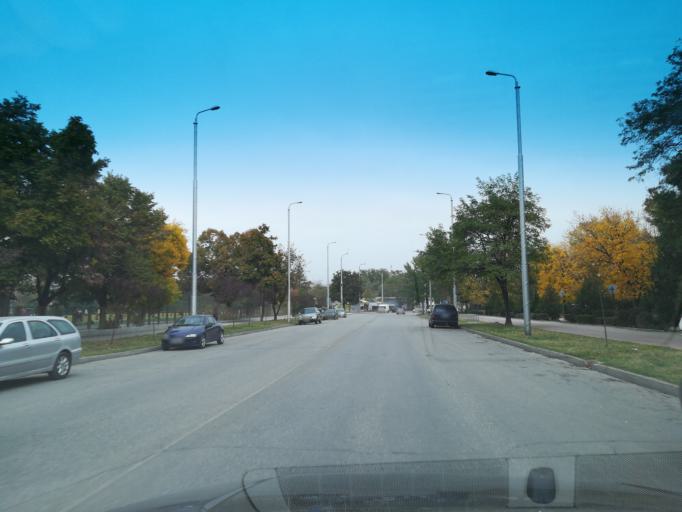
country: BG
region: Plovdiv
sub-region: Obshtina Plovdiv
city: Plovdiv
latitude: 42.1410
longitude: 24.7959
